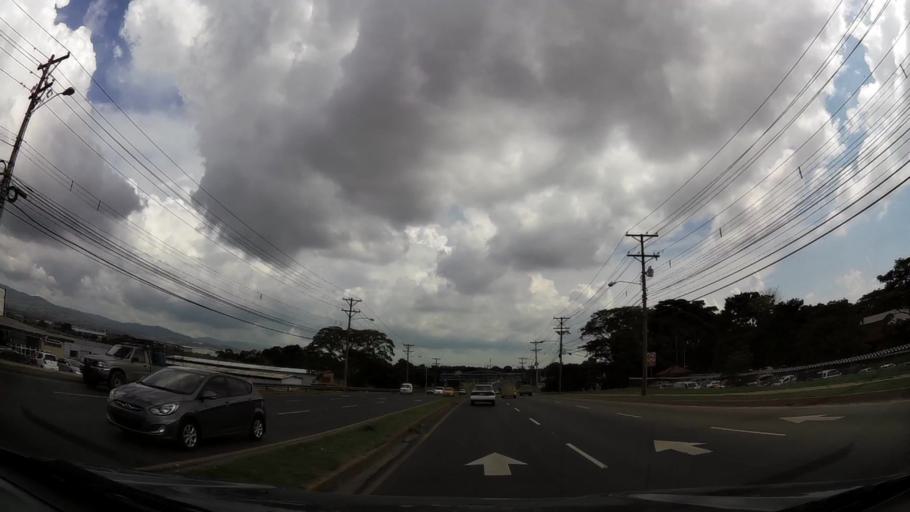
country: PA
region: Panama
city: Tocumen
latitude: 9.0665
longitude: -79.4127
